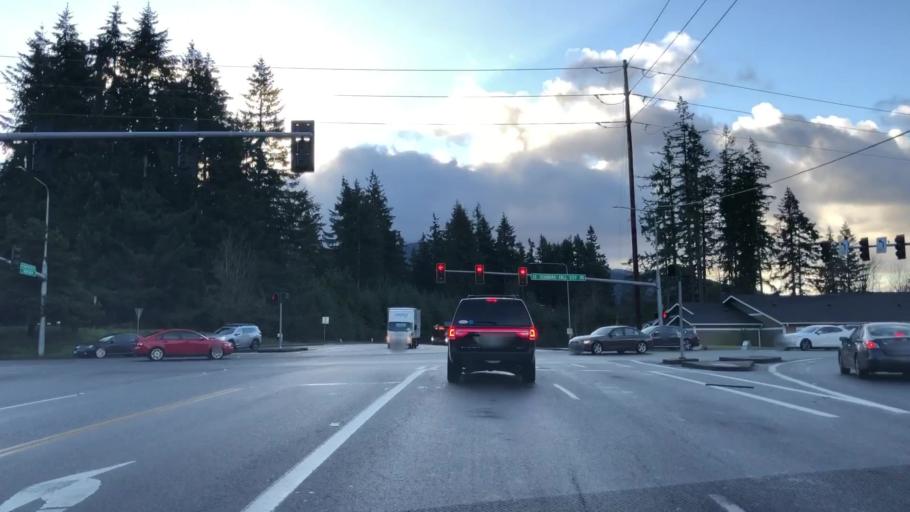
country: US
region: Washington
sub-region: King County
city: Issaquah
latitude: 47.5550
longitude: -122.0218
